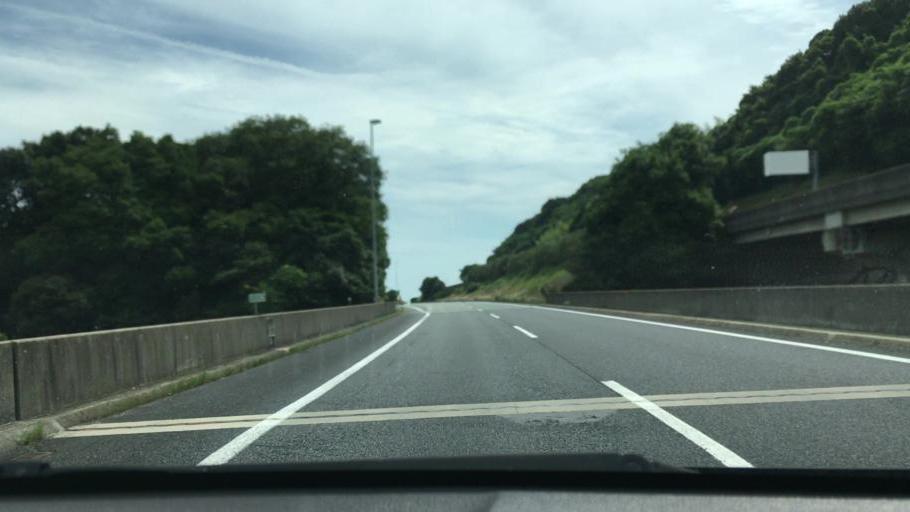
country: JP
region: Yamaguchi
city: Hofu
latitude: 34.0667
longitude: 131.6580
